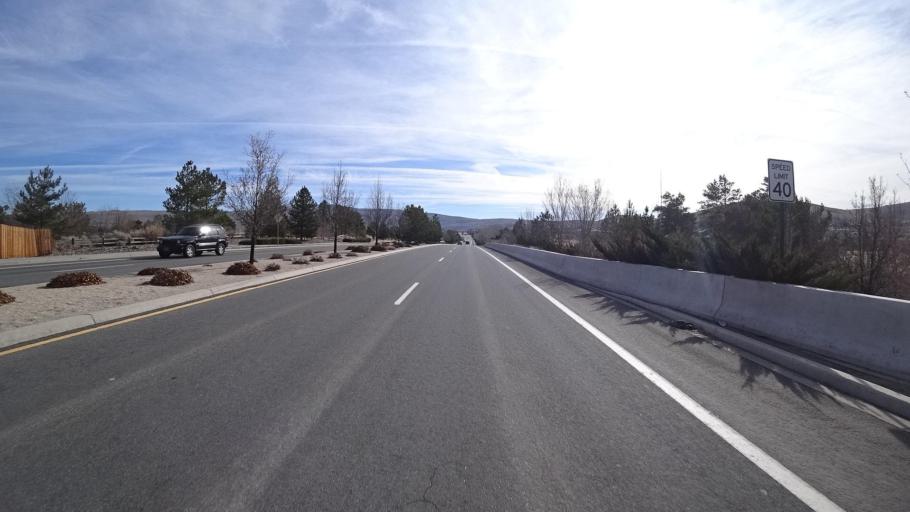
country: US
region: Nevada
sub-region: Washoe County
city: Spanish Springs
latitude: 39.6069
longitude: -119.6943
